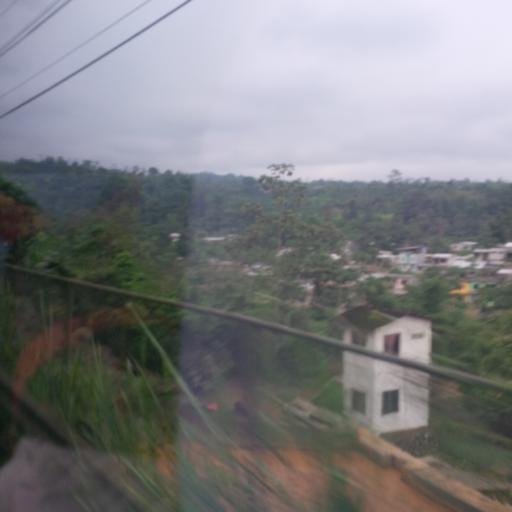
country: EC
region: Chimborazo
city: Alausi
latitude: -2.2023
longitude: -79.1270
